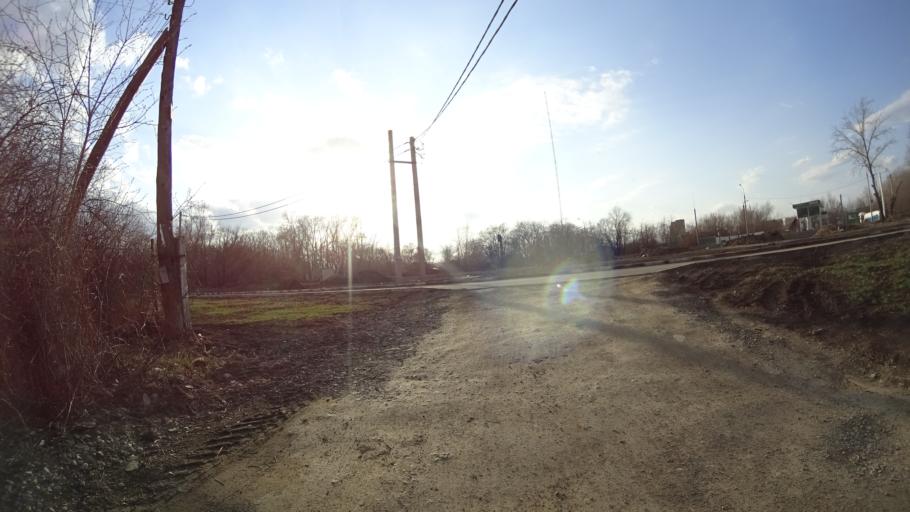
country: RU
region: Chelyabinsk
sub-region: Gorod Chelyabinsk
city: Chelyabinsk
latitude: 55.1342
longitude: 61.3895
